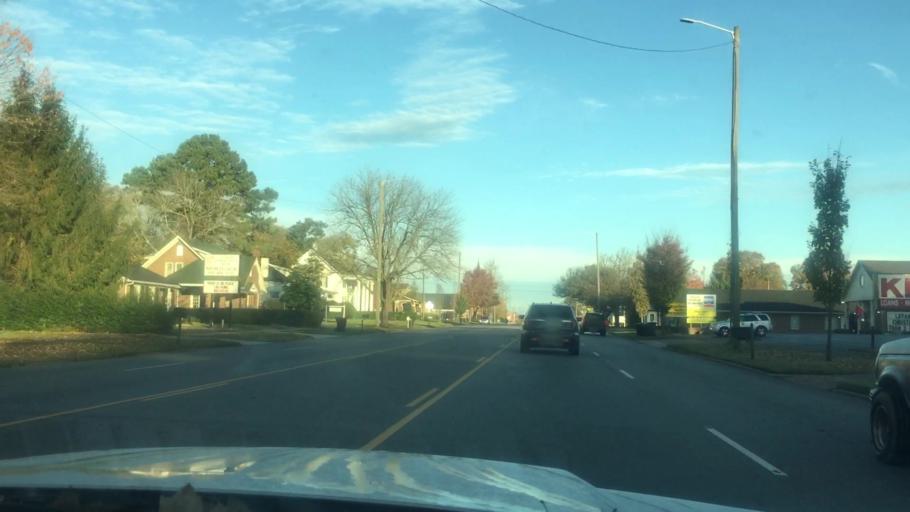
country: US
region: Tennessee
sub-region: Coffee County
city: Tullahoma
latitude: 35.3582
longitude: -86.2082
